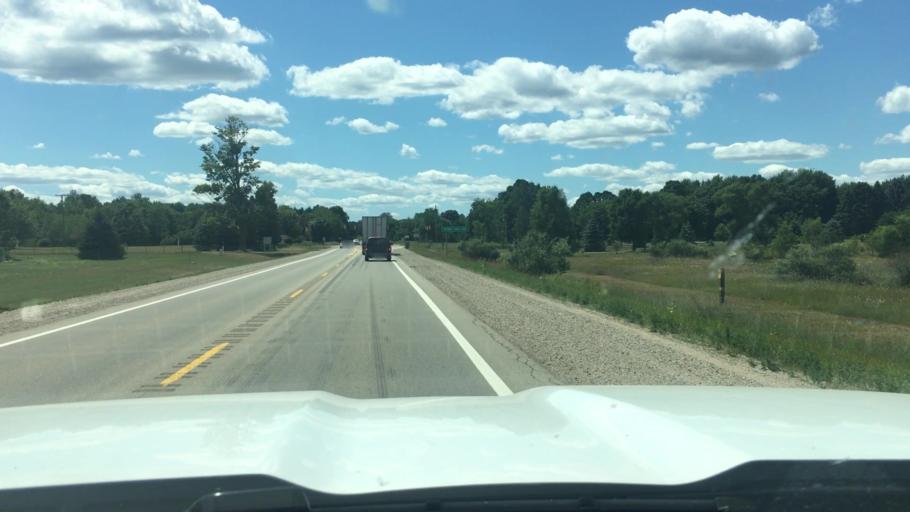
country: US
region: Michigan
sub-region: Kent County
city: Cedar Springs
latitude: 43.1758
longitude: -85.4874
